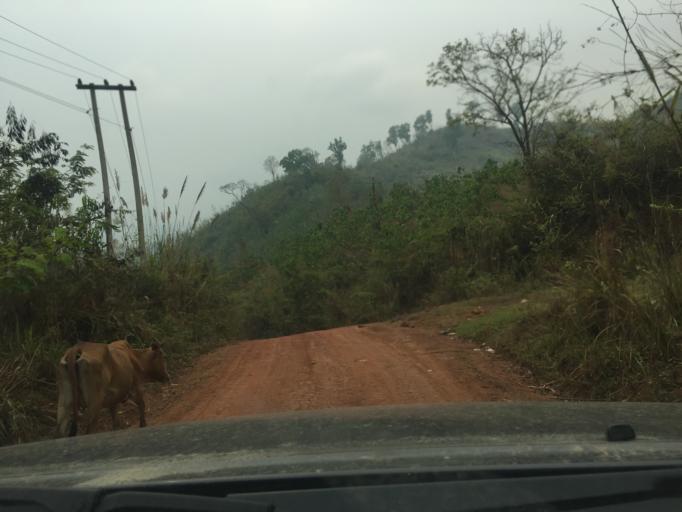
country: TH
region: Nan
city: Bo Kluea
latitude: 18.8582
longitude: 101.4266
